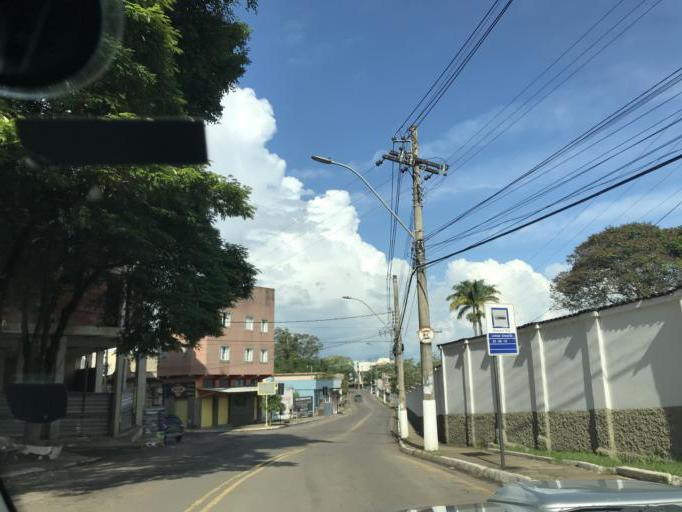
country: BR
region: Minas Gerais
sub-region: Tres Coracoes
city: Tres Coracoes
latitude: -21.7015
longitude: -45.2564
